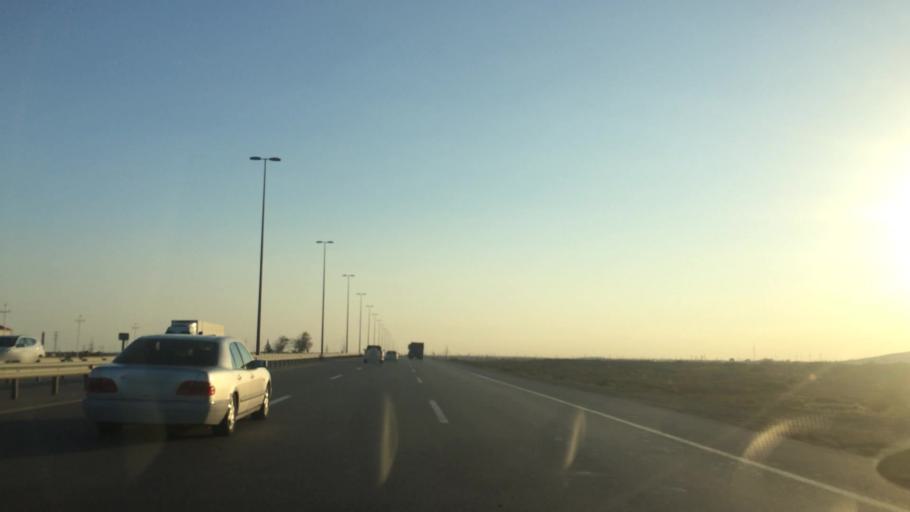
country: AZ
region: Baki
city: Qobustan
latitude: 39.9882
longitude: 49.4282
